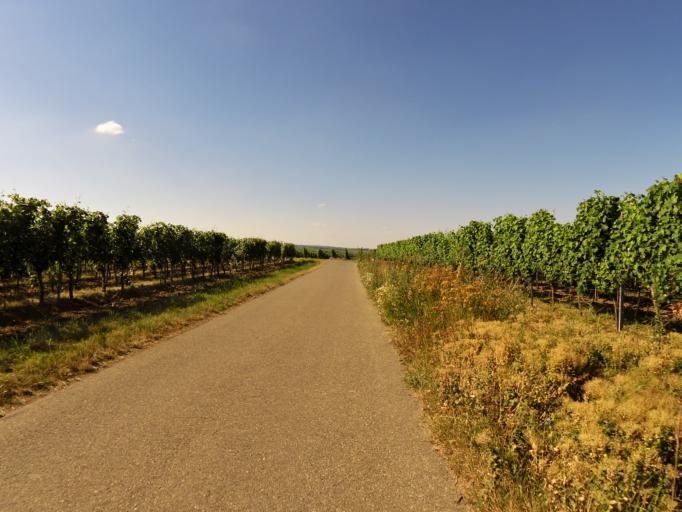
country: DE
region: Rheinland-Pfalz
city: Friedelsheim
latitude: 49.4606
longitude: 8.2062
